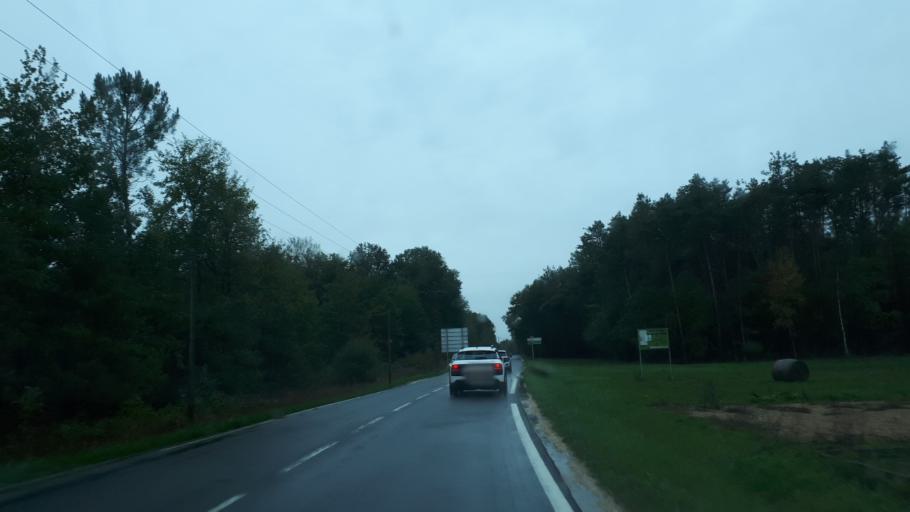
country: FR
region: Centre
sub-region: Departement du Loir-et-Cher
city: Gievres
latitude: 47.2954
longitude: 1.6719
